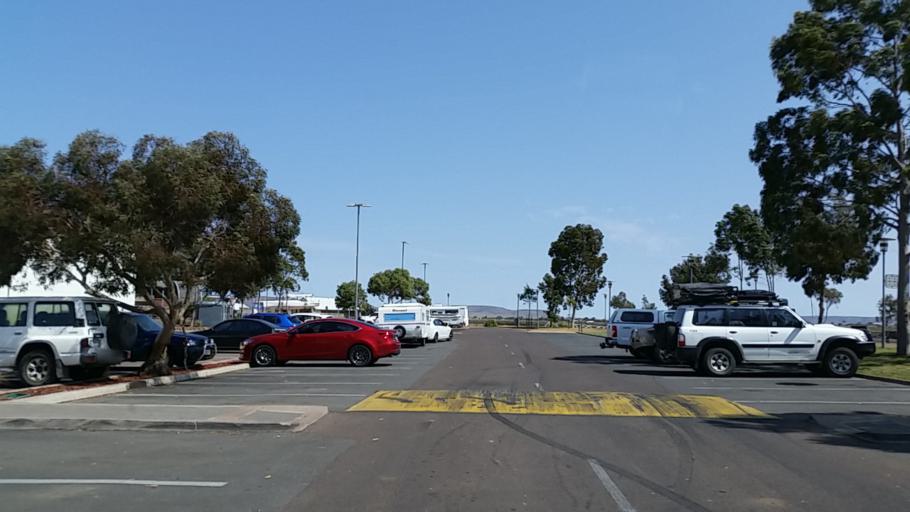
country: AU
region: South Australia
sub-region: Port Augusta
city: Port Augusta West
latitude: -32.4903
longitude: 137.7600
